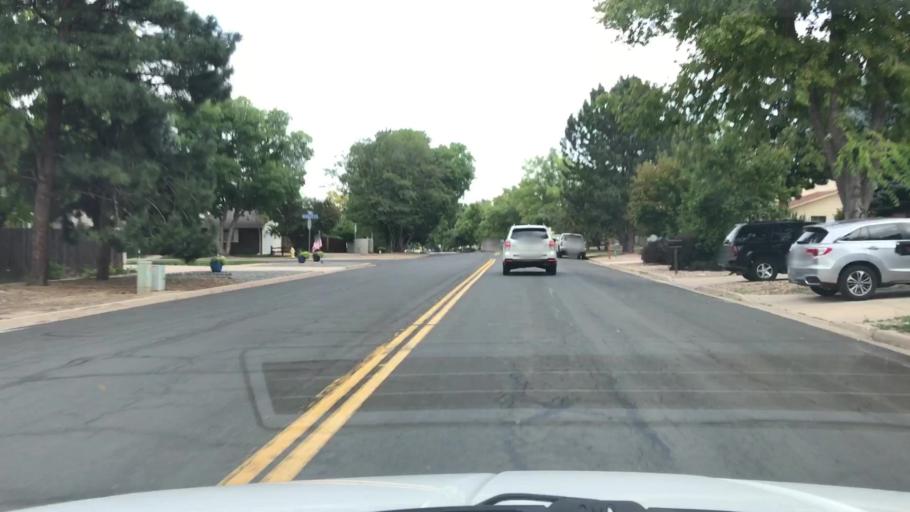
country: US
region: Colorado
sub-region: Broomfield County
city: Broomfield
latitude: 39.9329
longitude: -105.0807
